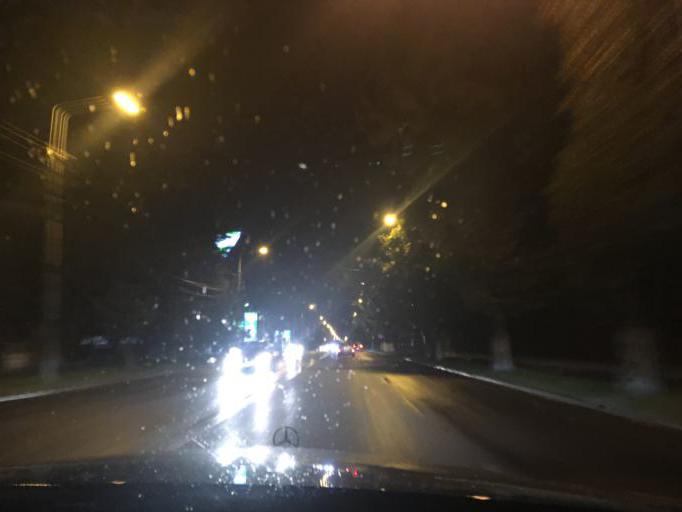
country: RO
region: Bihor
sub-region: Comuna Sanmartin
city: Sanmartin
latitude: 47.0407
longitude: 21.9769
